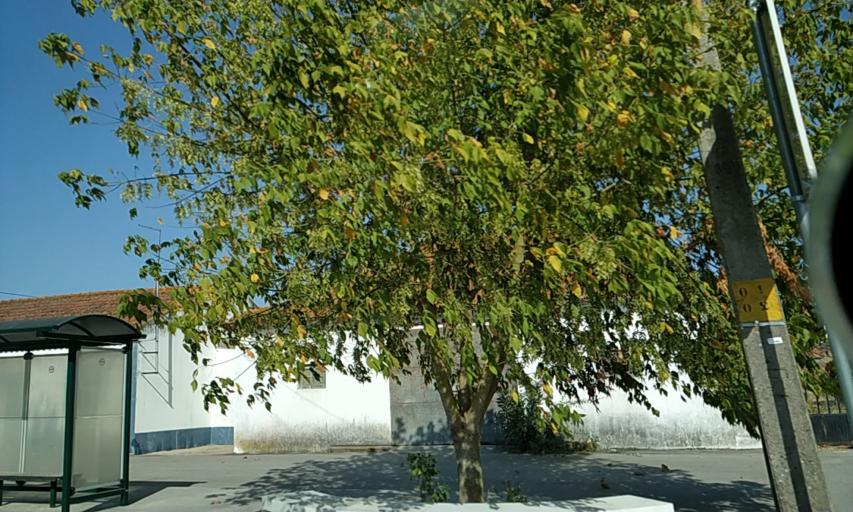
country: PT
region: Santarem
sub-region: Coruche
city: Coruche
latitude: 38.8879
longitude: -8.5348
